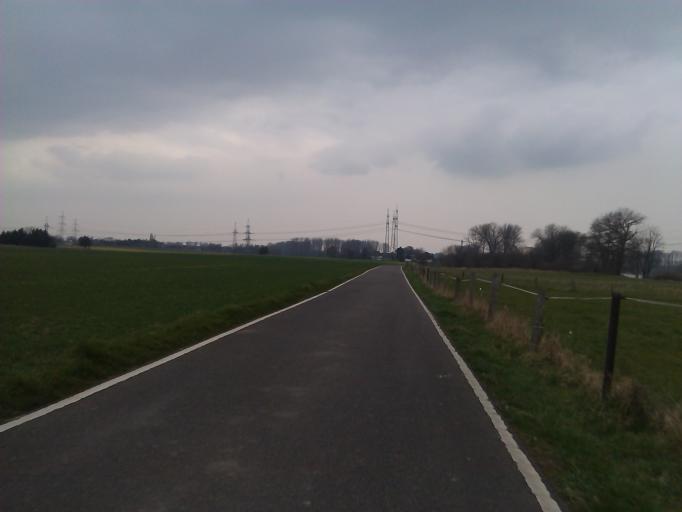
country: DE
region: North Rhine-Westphalia
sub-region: Regierungsbezirk Koln
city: Leverkusen
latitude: 51.0343
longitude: 6.9528
